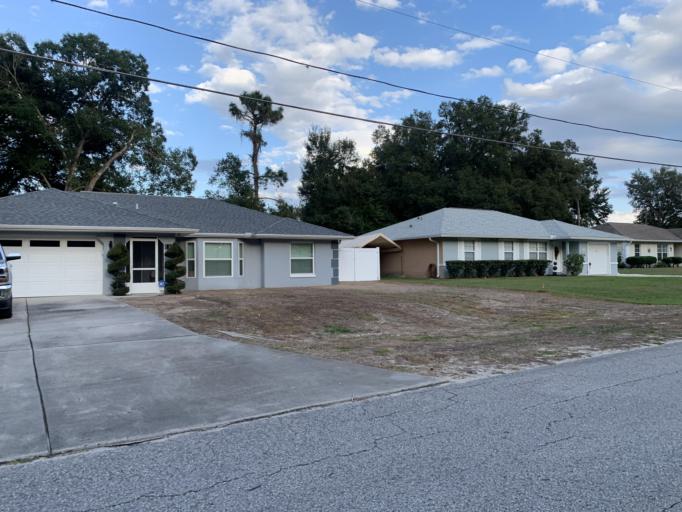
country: US
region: Florida
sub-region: Marion County
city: Silver Springs Shores
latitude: 29.1648
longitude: -82.0459
